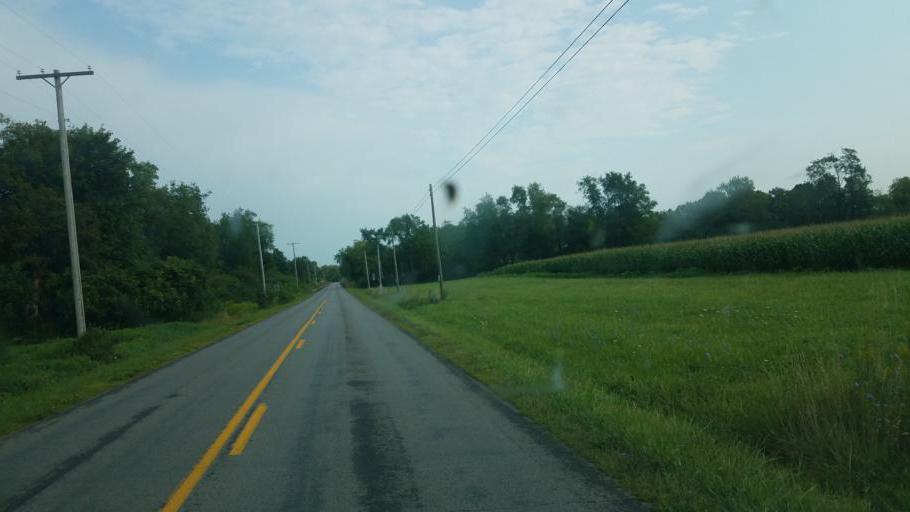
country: US
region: Pennsylvania
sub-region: Crawford County
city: Linesville
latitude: 41.6205
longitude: -80.4441
